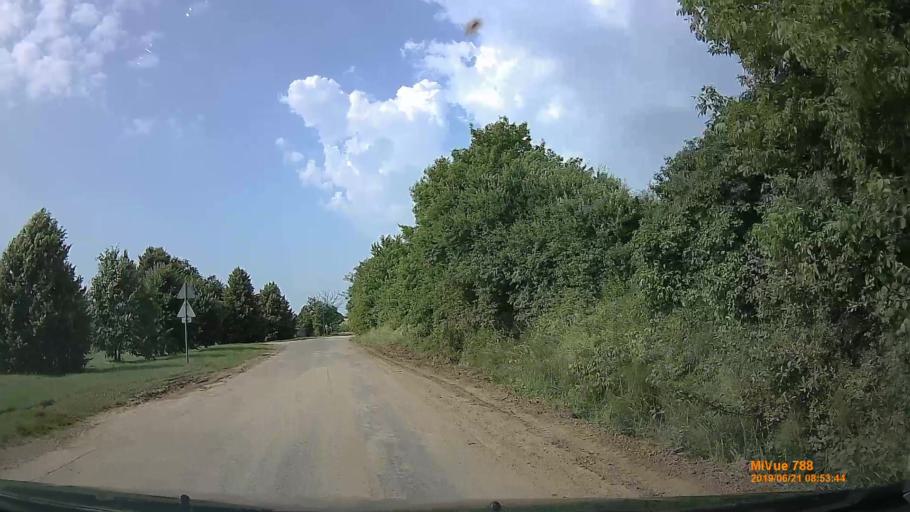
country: HU
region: Baranya
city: Buekkoesd
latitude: 46.1690
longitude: 17.8885
